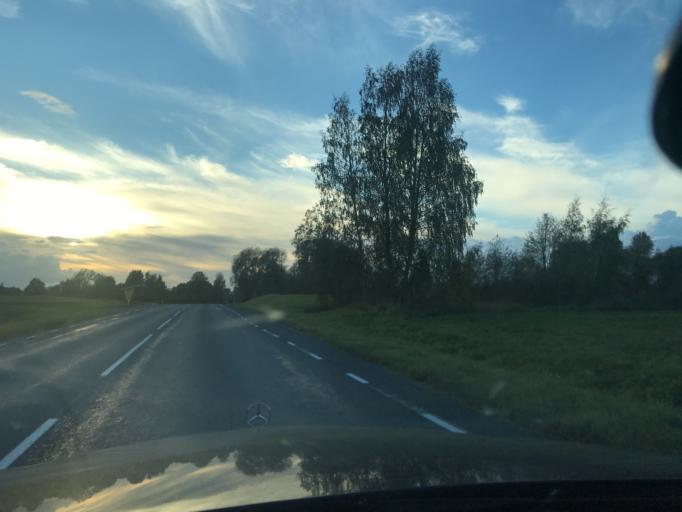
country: EE
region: Vorumaa
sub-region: Antsla vald
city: Vana-Antsla
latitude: 57.8776
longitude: 26.6599
